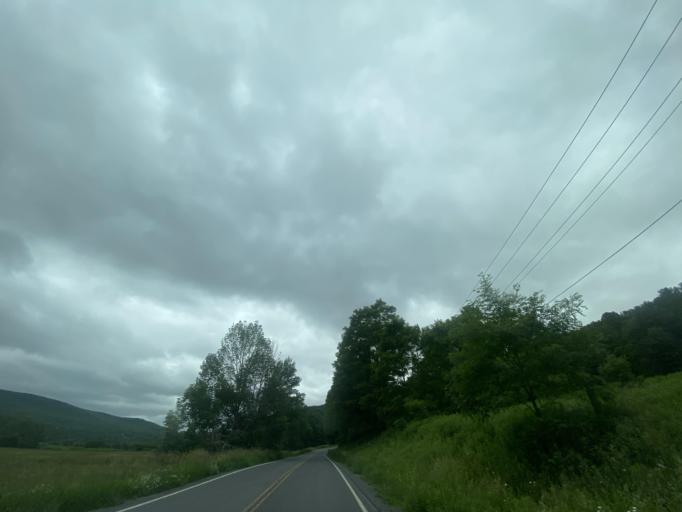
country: US
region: New York
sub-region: Schoharie County
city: Middleburgh
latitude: 42.3895
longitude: -74.3343
